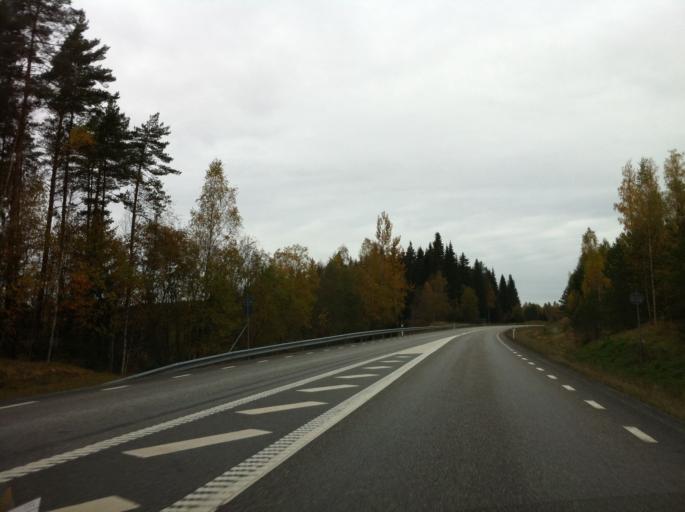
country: SE
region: OErebro
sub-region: Ljusnarsbergs Kommun
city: Kopparberg
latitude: 59.8690
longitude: 15.0510
